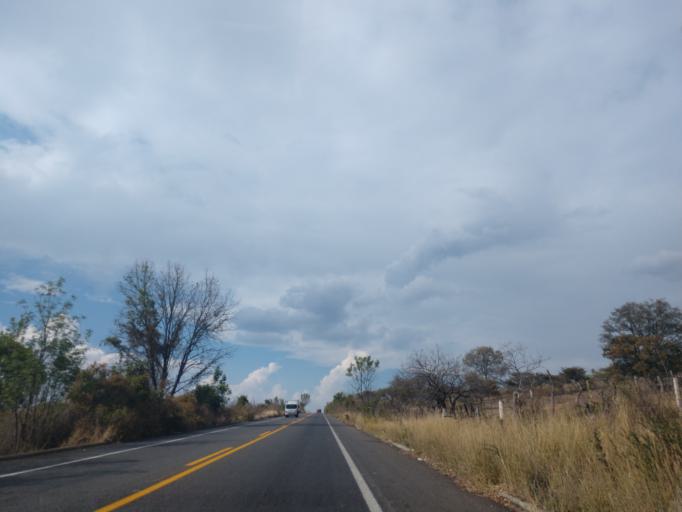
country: MX
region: Jalisco
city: La Manzanilla de la Paz
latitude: 20.0669
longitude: -103.1713
